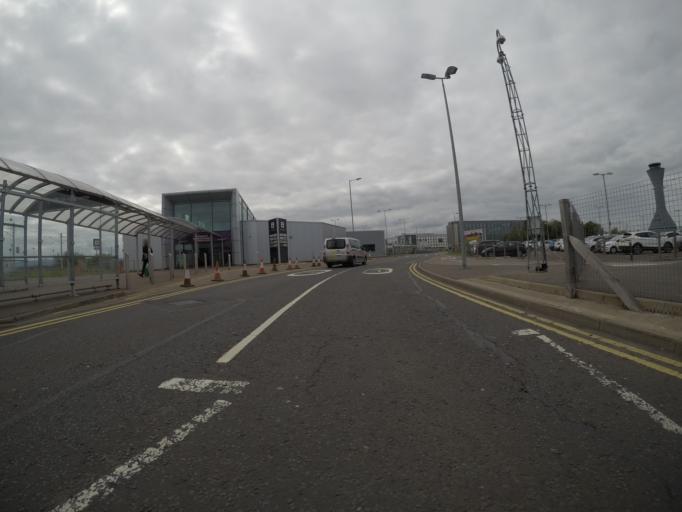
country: GB
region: Scotland
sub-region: Edinburgh
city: Ratho
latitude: 55.9467
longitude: -3.3601
